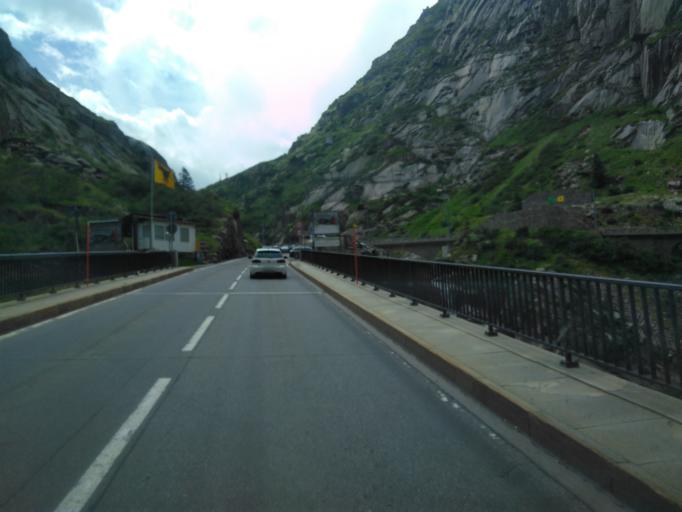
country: CH
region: Uri
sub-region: Uri
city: Andermatt
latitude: 46.6473
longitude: 8.5900
